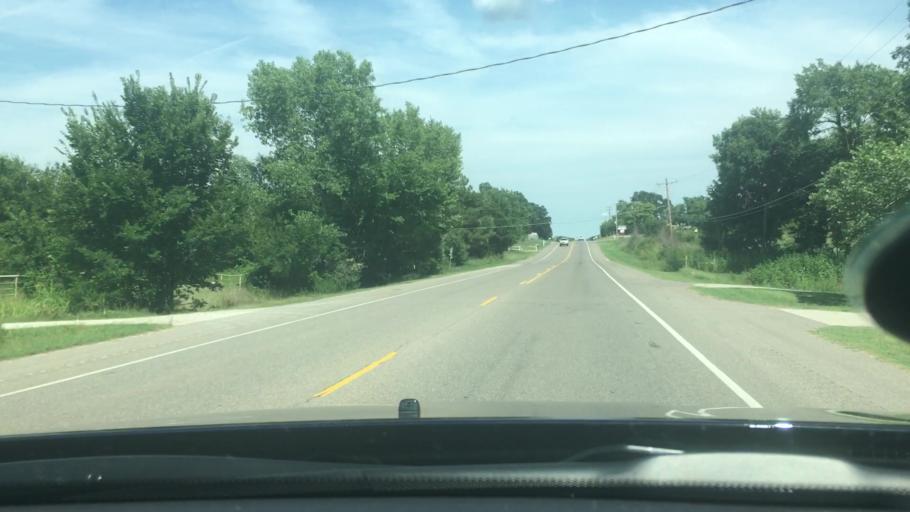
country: US
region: Oklahoma
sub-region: Pottawatomie County
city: Shawnee
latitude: 35.3331
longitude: -96.8545
